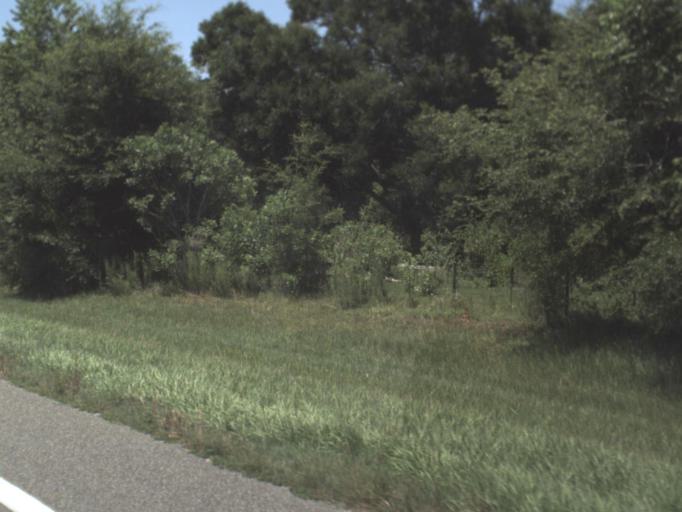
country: US
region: Florida
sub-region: Lafayette County
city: Mayo
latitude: 29.9613
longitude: -82.9694
